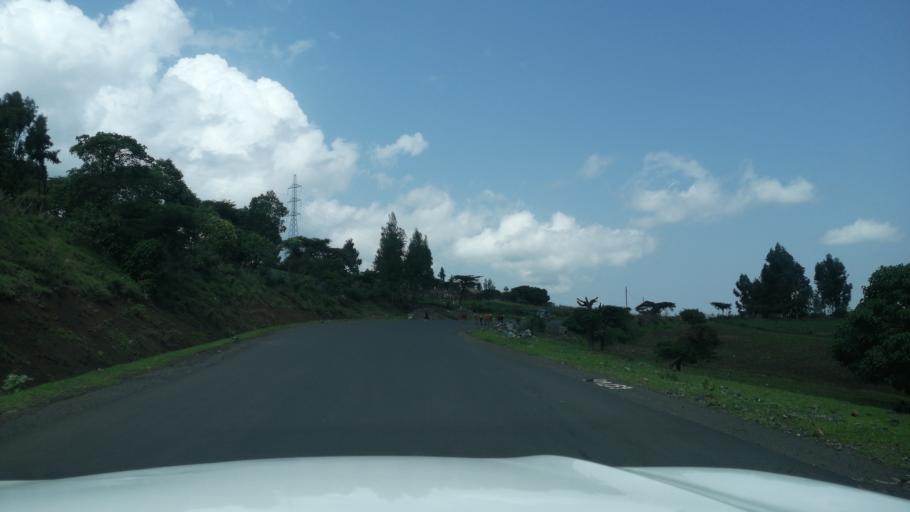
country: ET
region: Oromiya
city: Guder
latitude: 8.9909
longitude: 37.6122
